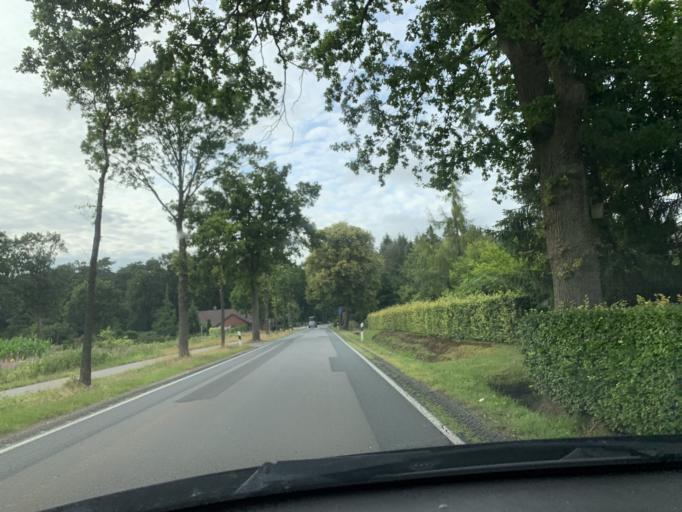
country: DE
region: Lower Saxony
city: Westerstede
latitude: 53.2861
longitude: 7.9228
